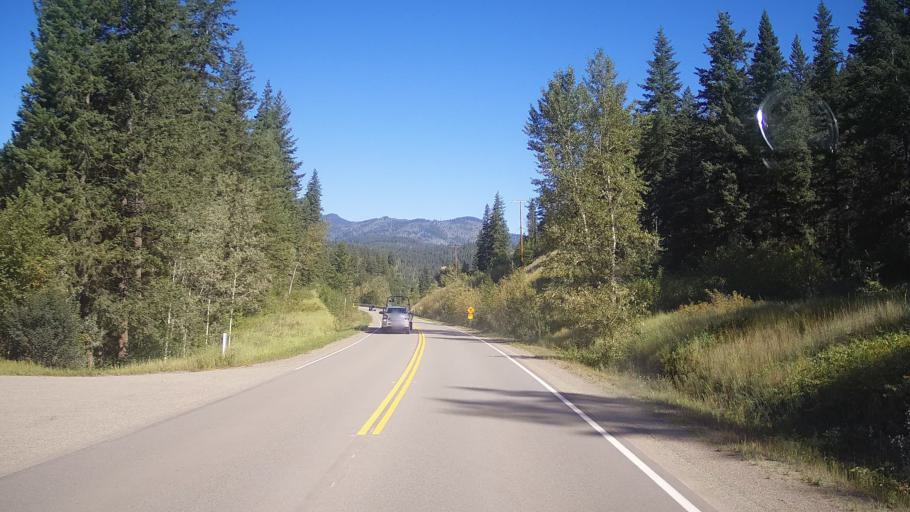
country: CA
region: British Columbia
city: Kamloops
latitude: 51.4510
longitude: -120.2143
